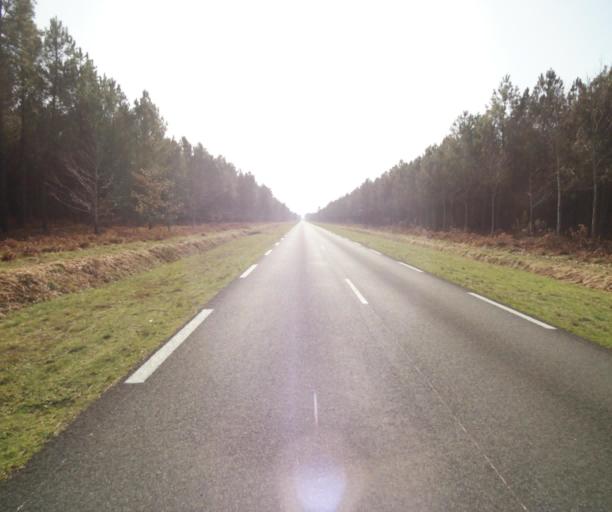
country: FR
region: Aquitaine
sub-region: Departement de la Gironde
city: Grignols
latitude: 44.1909
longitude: -0.1451
